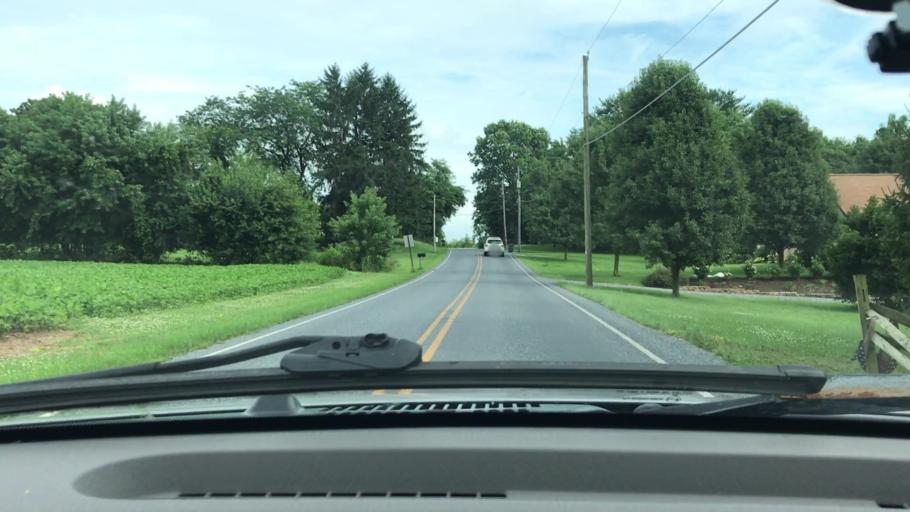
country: US
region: Pennsylvania
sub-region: Lancaster County
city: Elizabethtown
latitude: 40.1654
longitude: -76.5809
